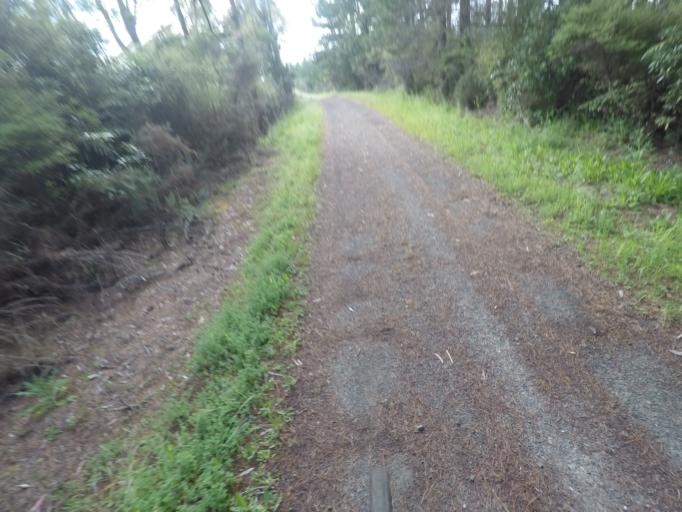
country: NZ
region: Auckland
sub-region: Auckland
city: Parakai
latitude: -36.7088
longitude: 174.5816
